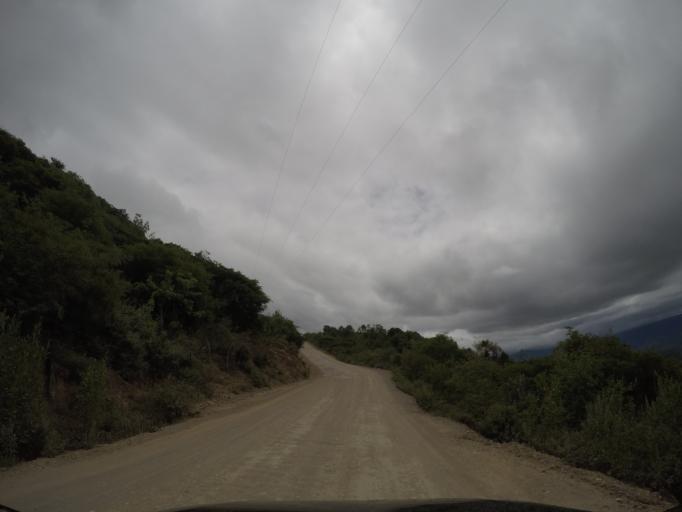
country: MX
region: Oaxaca
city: San Lorenzo Albarradas
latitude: 16.8885
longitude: -96.2654
